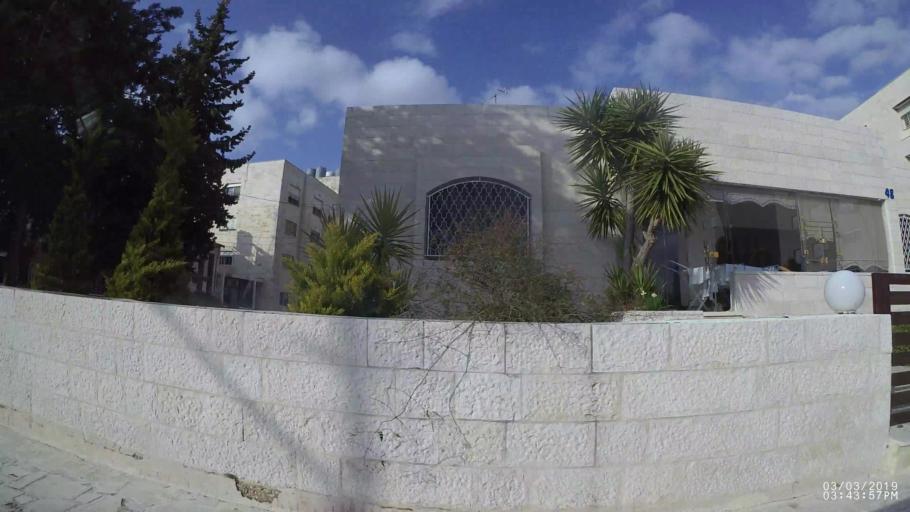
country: JO
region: Amman
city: Al Jubayhah
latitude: 31.9838
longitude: 35.8786
